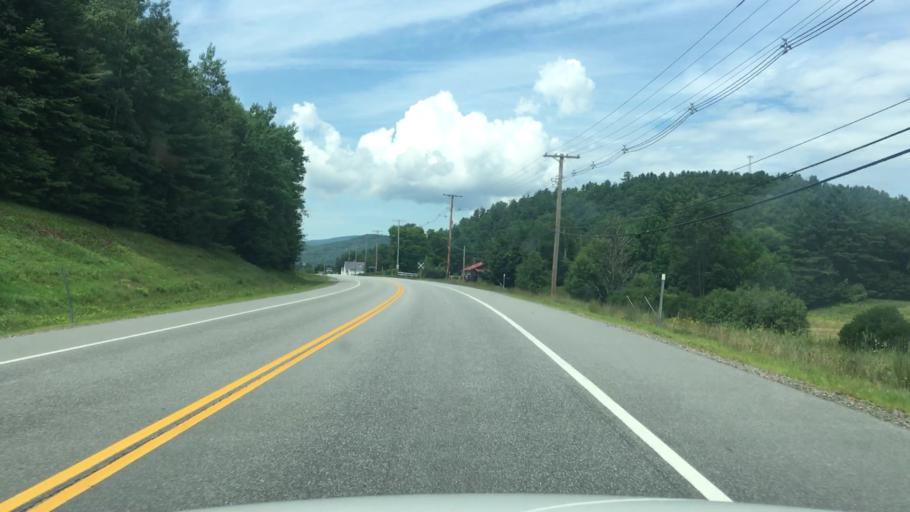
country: US
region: New Hampshire
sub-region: Grafton County
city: Rumney
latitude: 43.8179
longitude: -71.8786
